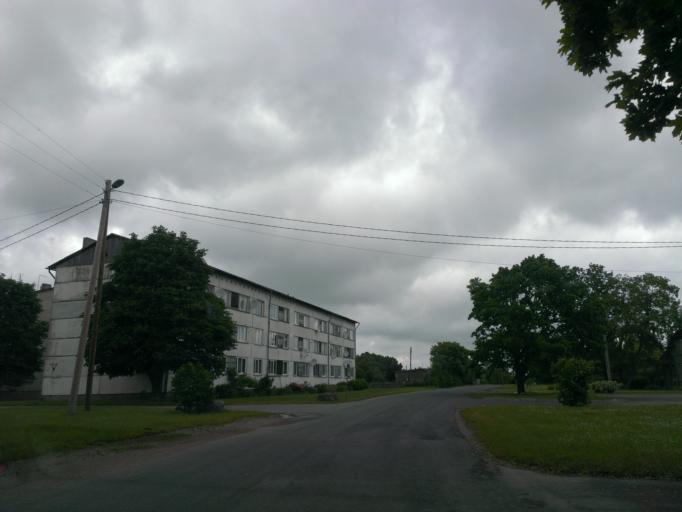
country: LV
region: Durbe
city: Liegi
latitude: 56.7374
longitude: 21.3863
